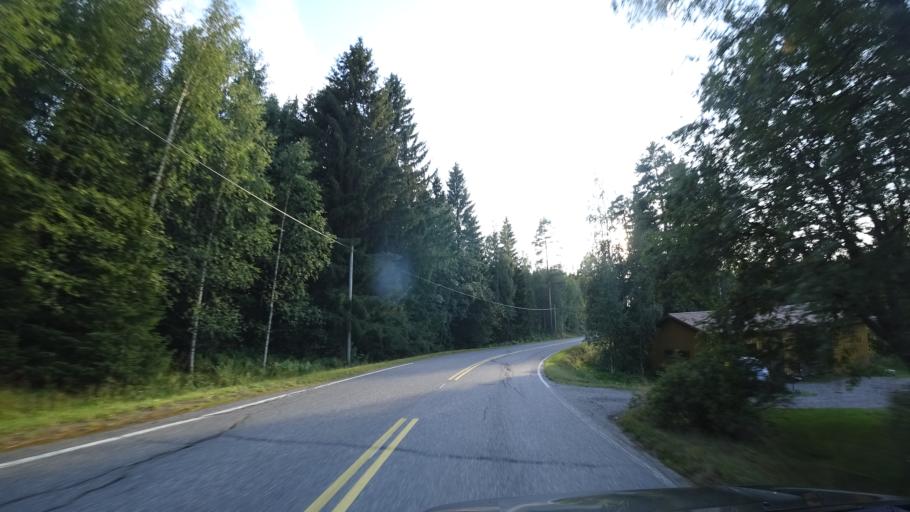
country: FI
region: Haeme
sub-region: Haemeenlinna
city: Lammi
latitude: 61.0631
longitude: 24.9878
